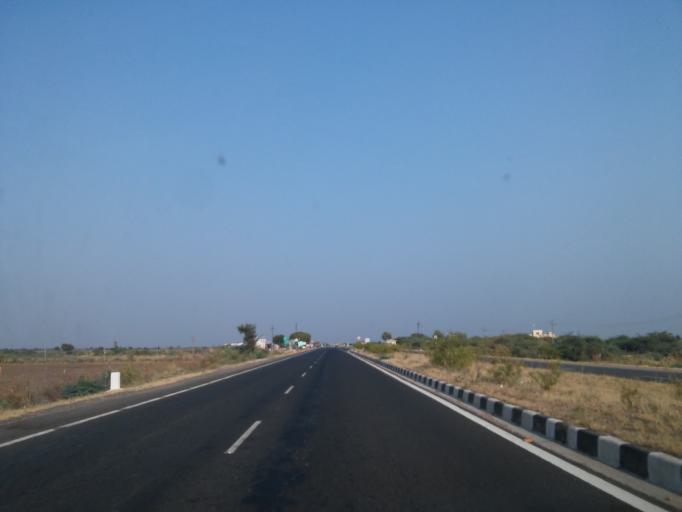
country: IN
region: Gujarat
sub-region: Surendranagar
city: Dhrangadhra
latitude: 23.0287
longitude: 71.6504
